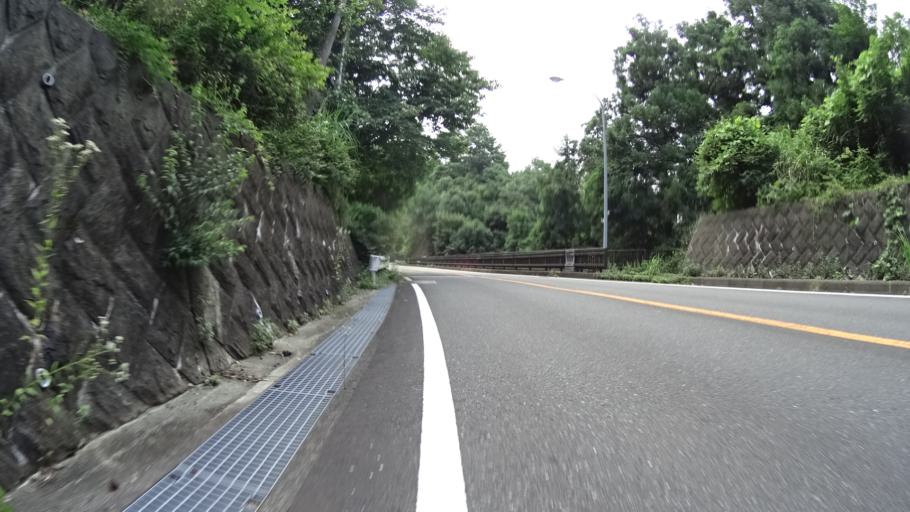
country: JP
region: Kanagawa
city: Hadano
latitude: 35.5167
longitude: 139.2321
